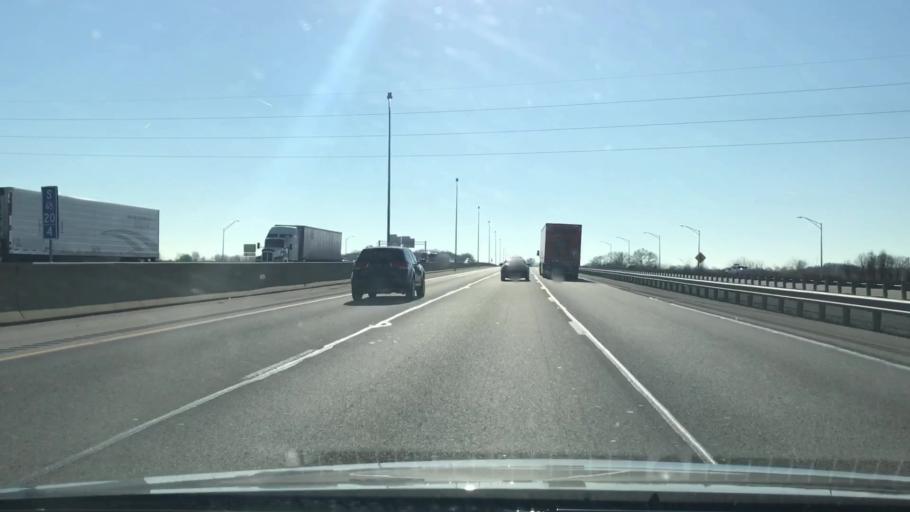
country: US
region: Kentucky
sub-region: Warren County
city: Plano
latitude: 36.9072
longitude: -86.4342
